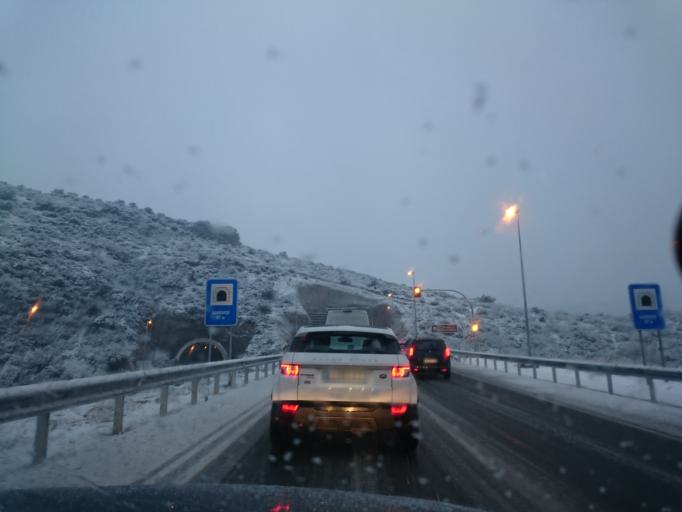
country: ES
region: Catalonia
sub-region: Provincia de Barcelona
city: Vilafranca del Penedes
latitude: 41.3064
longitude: 1.7218
